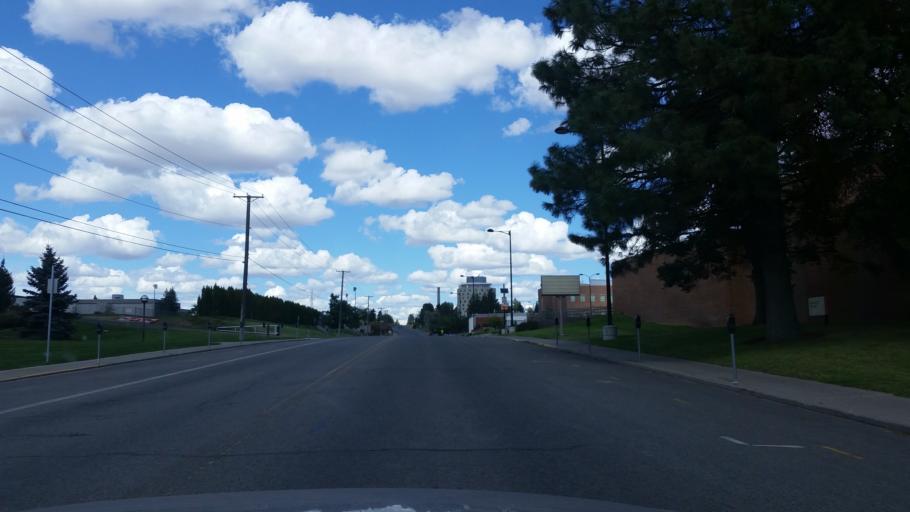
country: US
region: Washington
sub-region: Spokane County
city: Cheney
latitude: 47.4875
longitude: -117.5863
